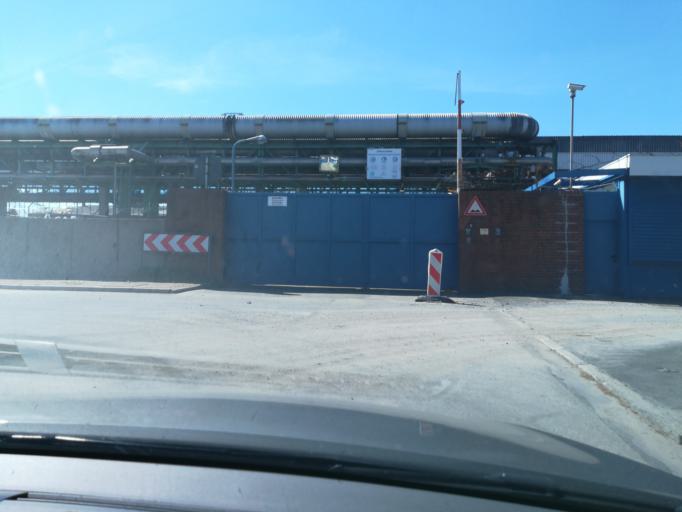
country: DE
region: Hamburg
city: Rothenburgsort
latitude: 53.5159
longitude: 10.0396
